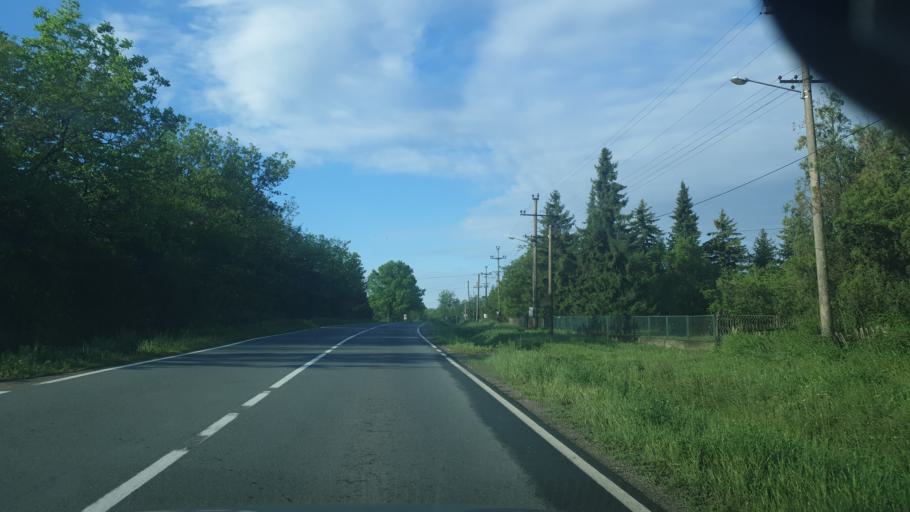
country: RS
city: Stubline
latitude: 44.5988
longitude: 20.1471
